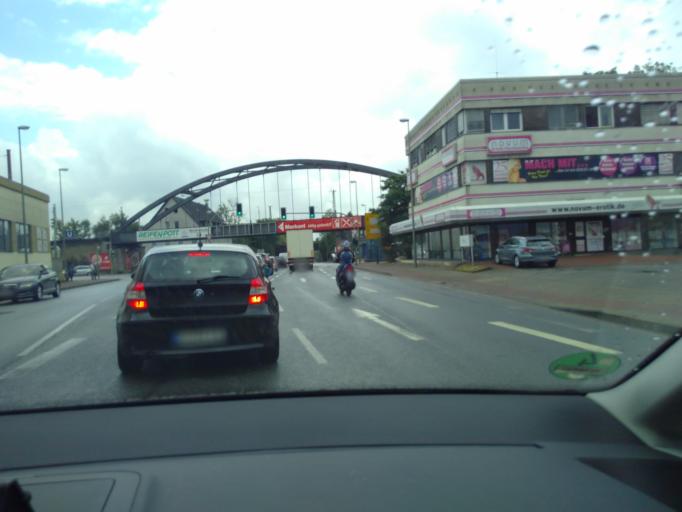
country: DE
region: North Rhine-Westphalia
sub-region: Regierungsbezirk Detmold
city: Bielefeld
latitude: 52.0326
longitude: 8.5433
